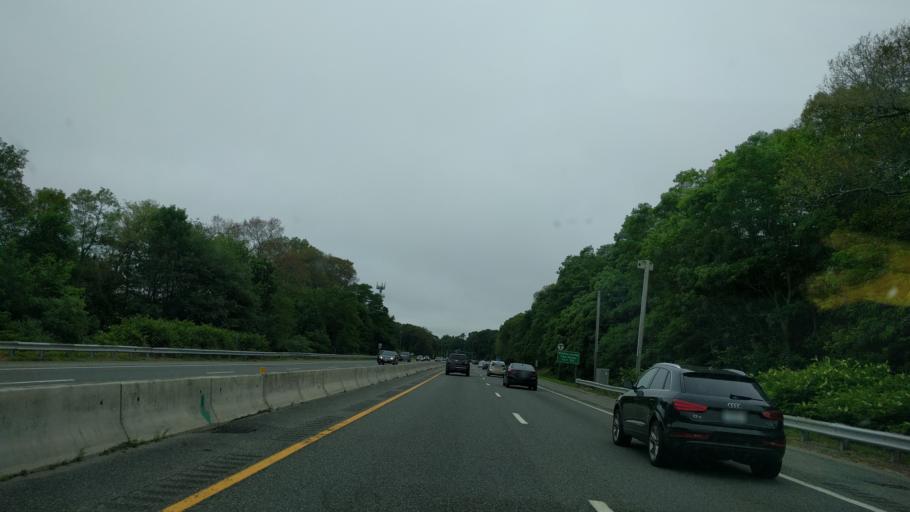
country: US
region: Rhode Island
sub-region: Washington County
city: Exeter
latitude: 41.5916
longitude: -71.5005
